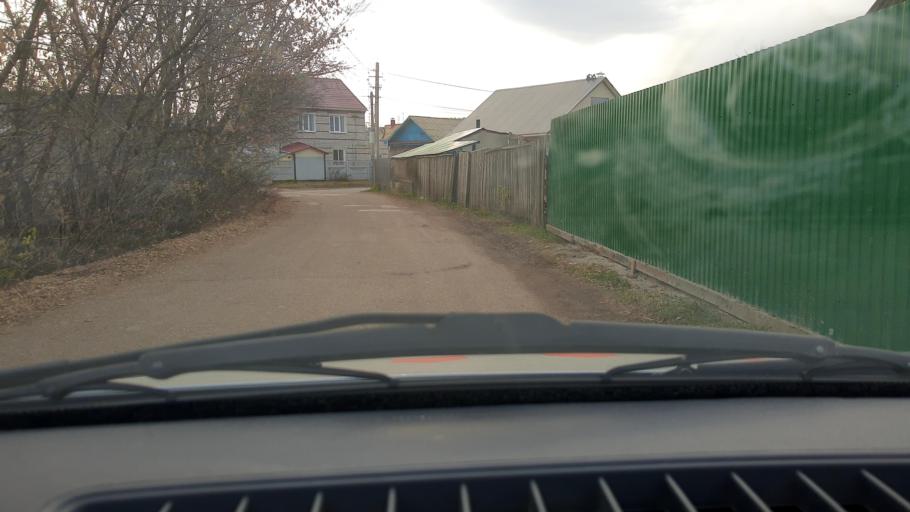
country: RU
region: Bashkortostan
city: Ufa
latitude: 54.7378
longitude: 55.9063
